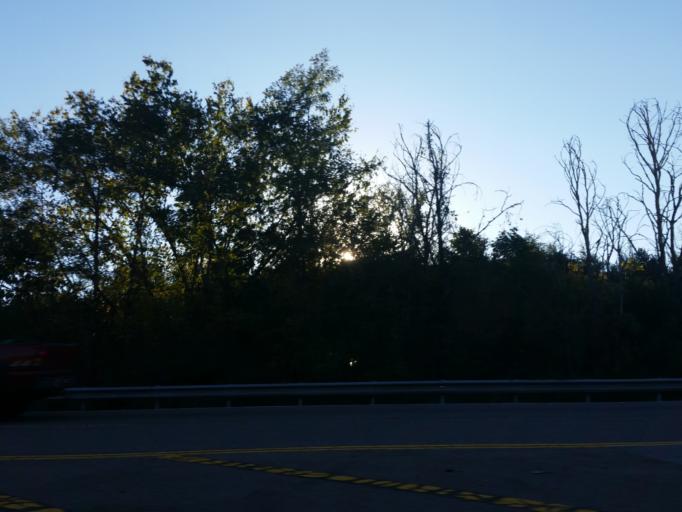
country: US
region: Tennessee
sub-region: Grainger County
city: Rutledge
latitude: 36.3517
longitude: -83.4348
